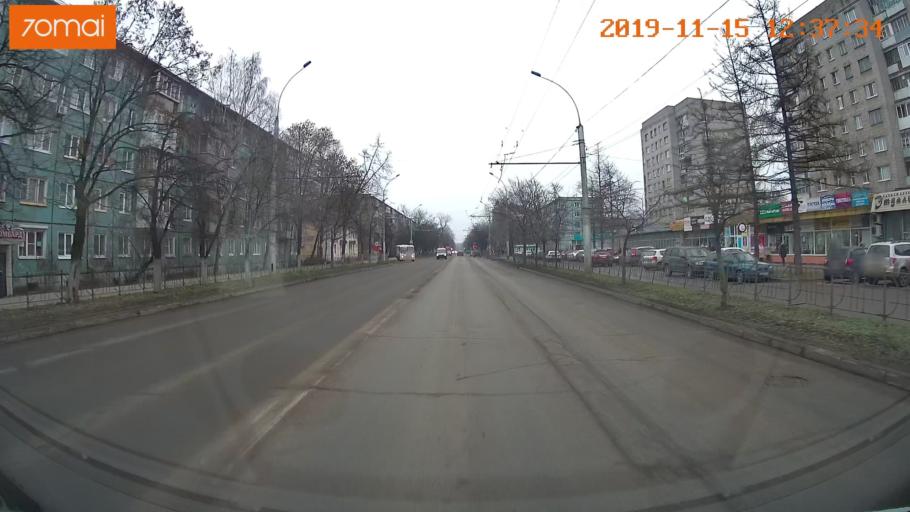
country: RU
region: Vologda
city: Vologda
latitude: 59.2082
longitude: 39.9003
